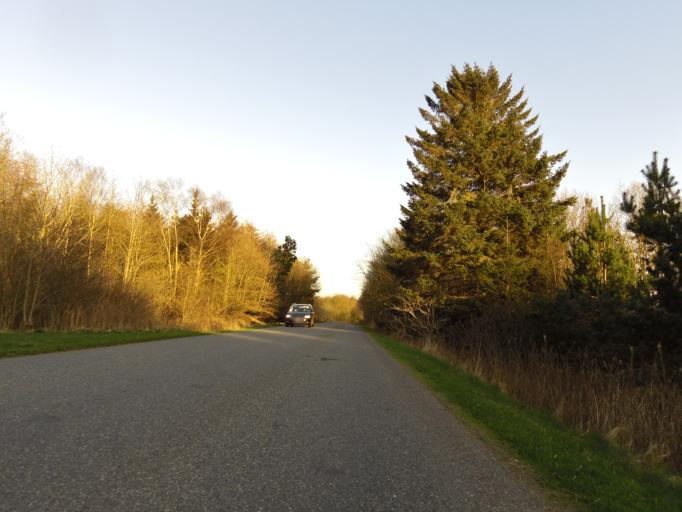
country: DK
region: Central Jutland
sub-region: Holstebro Kommune
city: Vinderup
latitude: 56.5191
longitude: 8.7914
